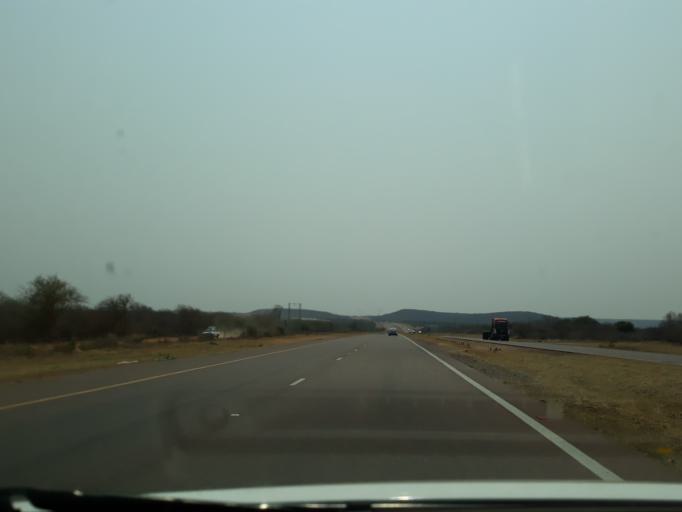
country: BW
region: Kgatleng
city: Bokaa
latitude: -24.4115
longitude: 26.0510
